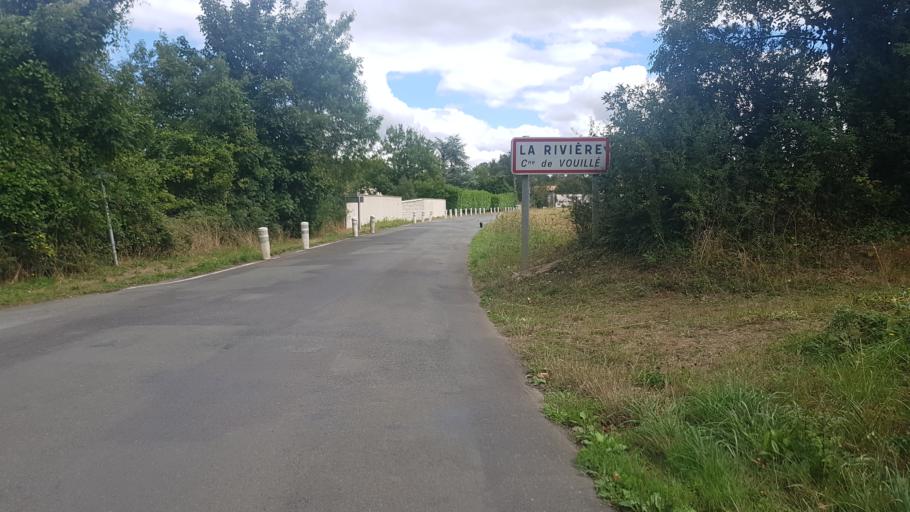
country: FR
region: Poitou-Charentes
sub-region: Departement des Deux-Sevres
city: Vouille
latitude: 46.3284
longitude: -0.3476
